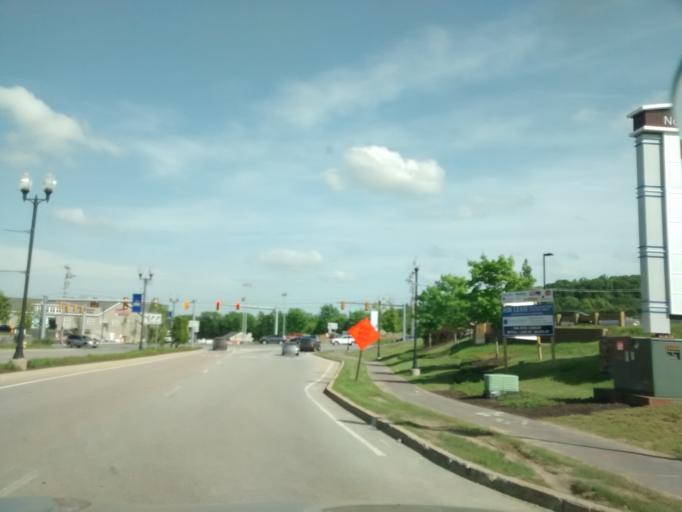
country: US
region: Massachusetts
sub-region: Worcester County
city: Northborough
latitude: 42.2863
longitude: -71.6693
